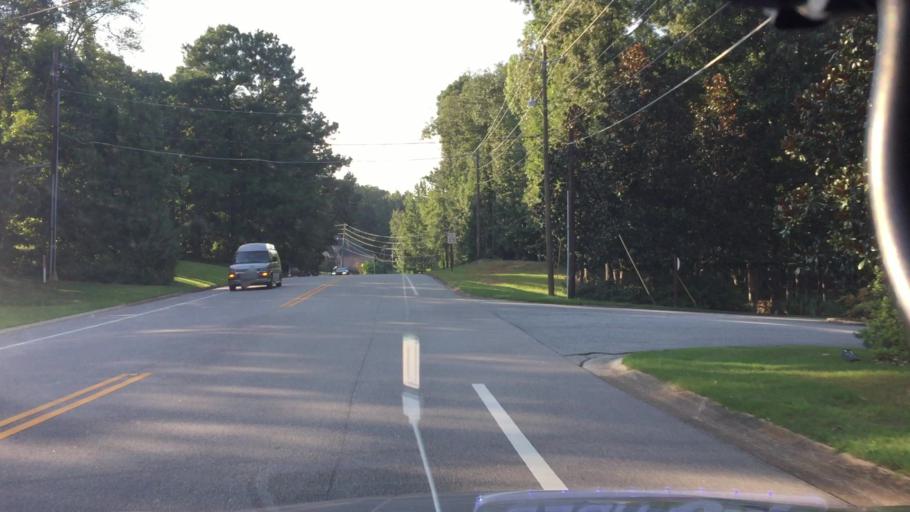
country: US
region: Alabama
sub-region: Lee County
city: Opelika
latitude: 32.5979
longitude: -85.4179
